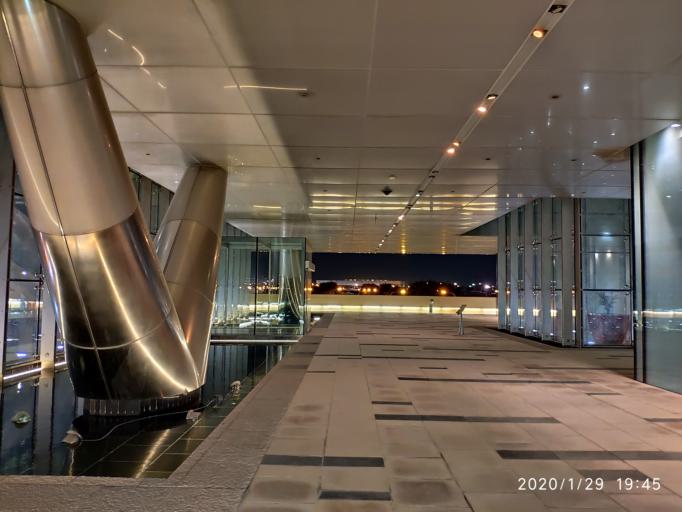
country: QA
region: Baladiyat ar Rayyan
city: Ar Rayyan
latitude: 25.3253
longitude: 51.4379
